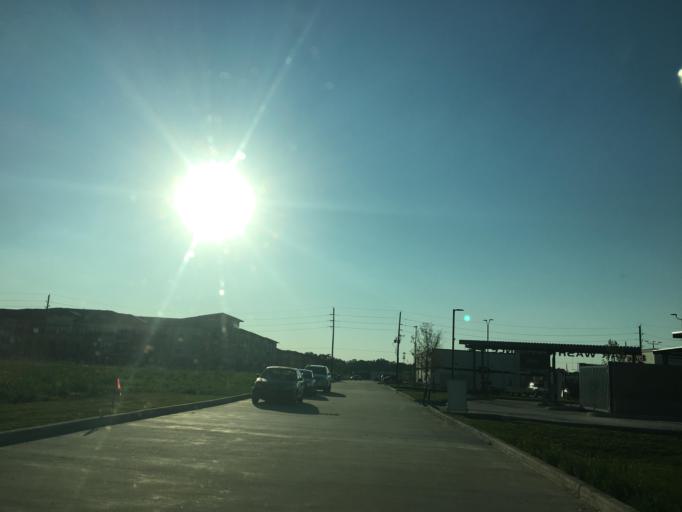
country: US
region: Texas
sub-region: Harris County
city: Spring
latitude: 30.0821
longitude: -95.4434
